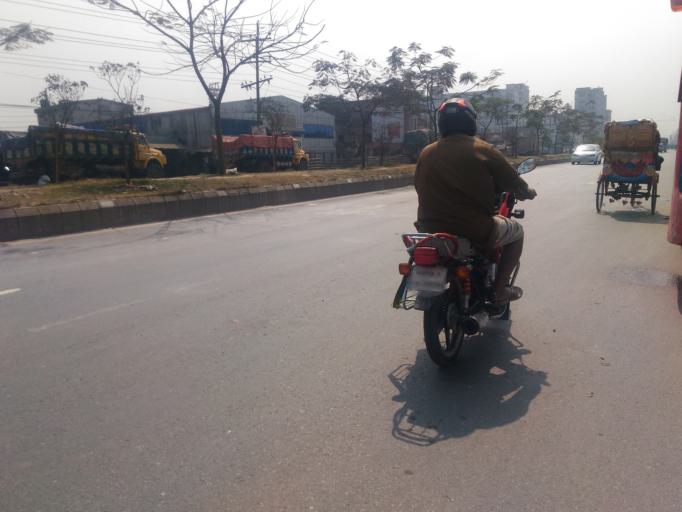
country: BD
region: Dhaka
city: Tungi
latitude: 24.0037
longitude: 90.3831
